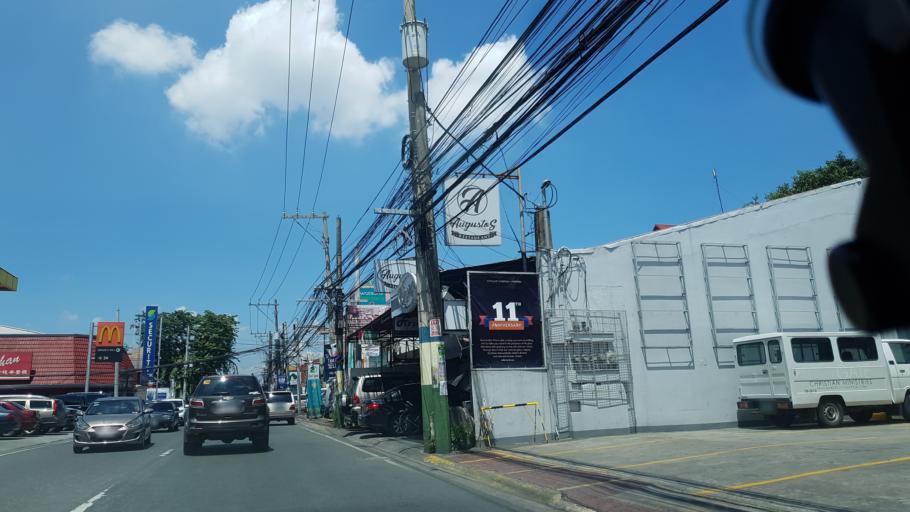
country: PH
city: Sambayanihan People's Village
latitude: 14.4469
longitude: 121.0291
